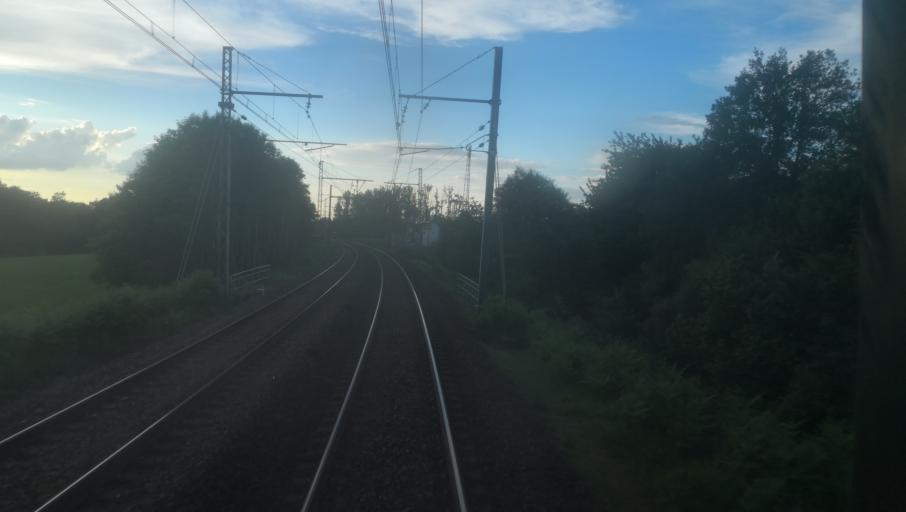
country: FR
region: Limousin
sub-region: Departement de la Creuse
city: Saint-Agnant-de-Versillat
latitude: 46.3390
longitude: 1.5385
